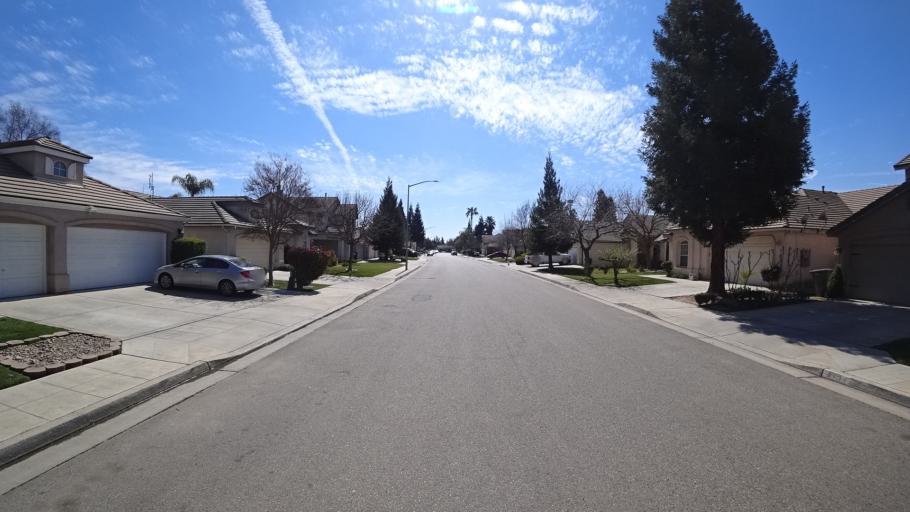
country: US
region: California
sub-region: Fresno County
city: Clovis
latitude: 36.8540
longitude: -119.7686
